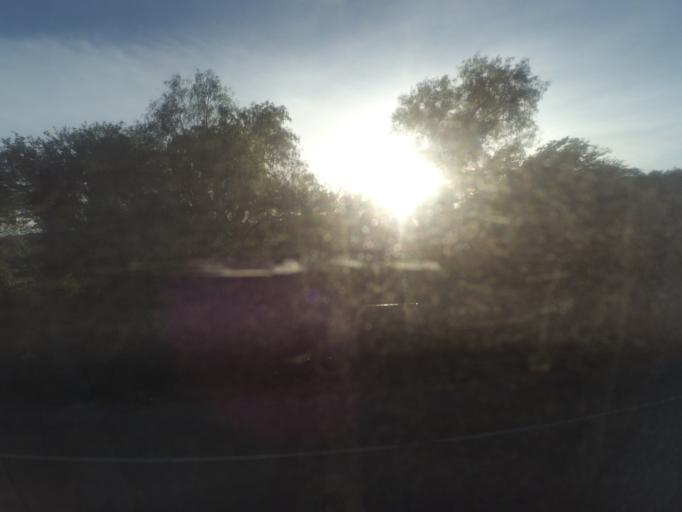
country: BO
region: Tarija
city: Tarija
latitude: -21.5260
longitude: -64.5743
